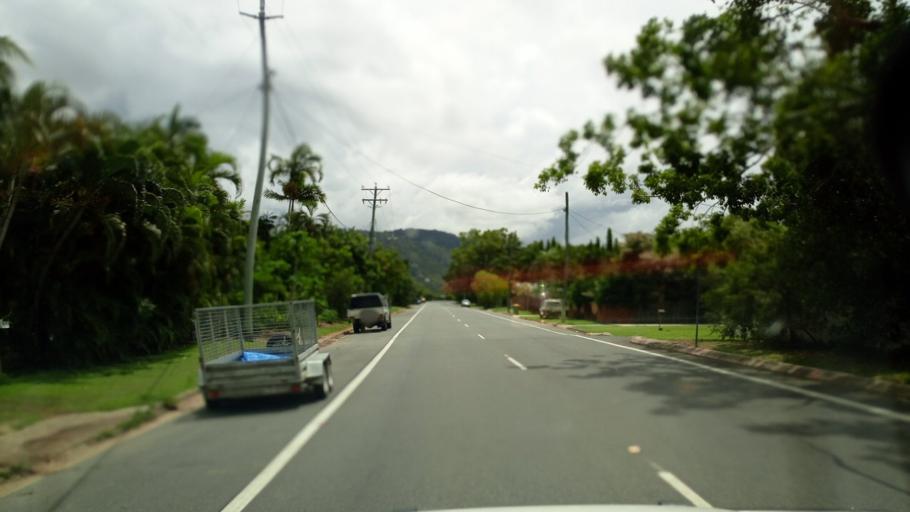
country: AU
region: Queensland
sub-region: Cairns
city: Redlynch
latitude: -16.8538
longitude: 145.7430
